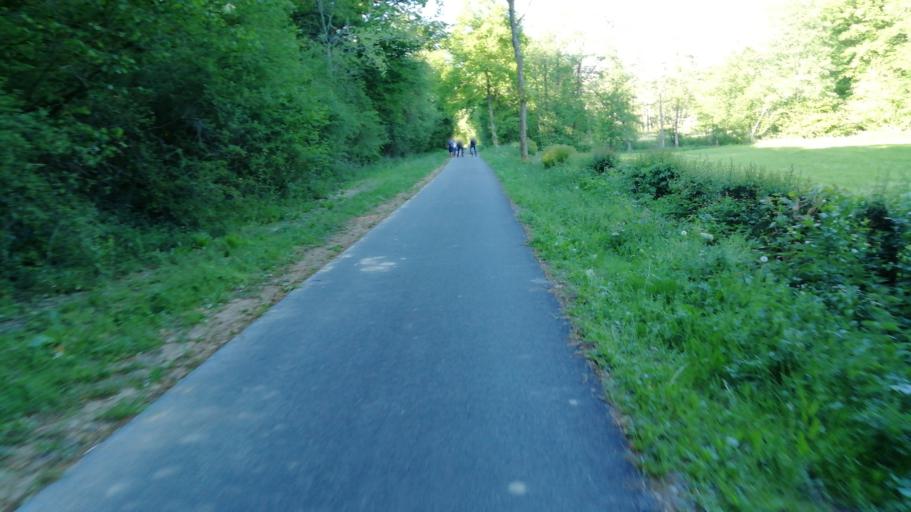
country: FR
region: Nord-Pas-de-Calais
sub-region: Departement du Nord
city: Ferriere-la-Grande
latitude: 50.2041
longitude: 4.0302
